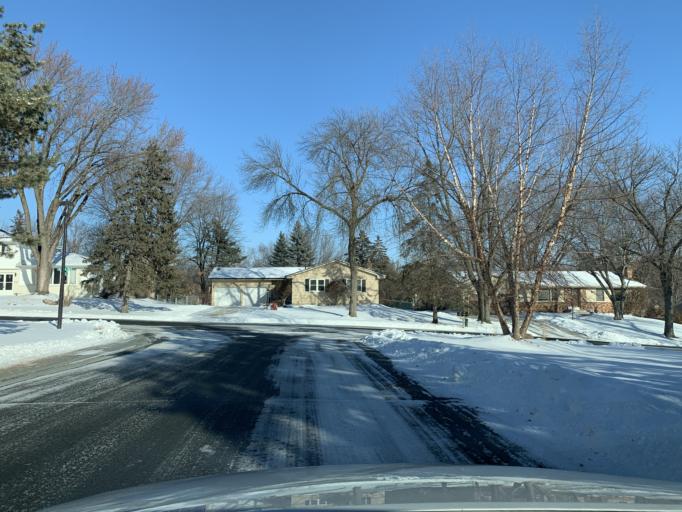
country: US
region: Minnesota
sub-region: Scott County
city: Savage
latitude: 44.8218
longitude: -93.3400
